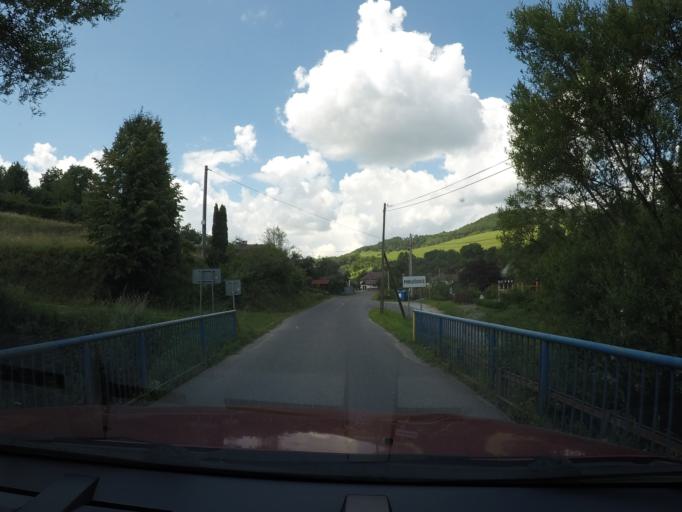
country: SK
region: Kosicky
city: Gelnica
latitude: 48.9146
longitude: 21.0847
